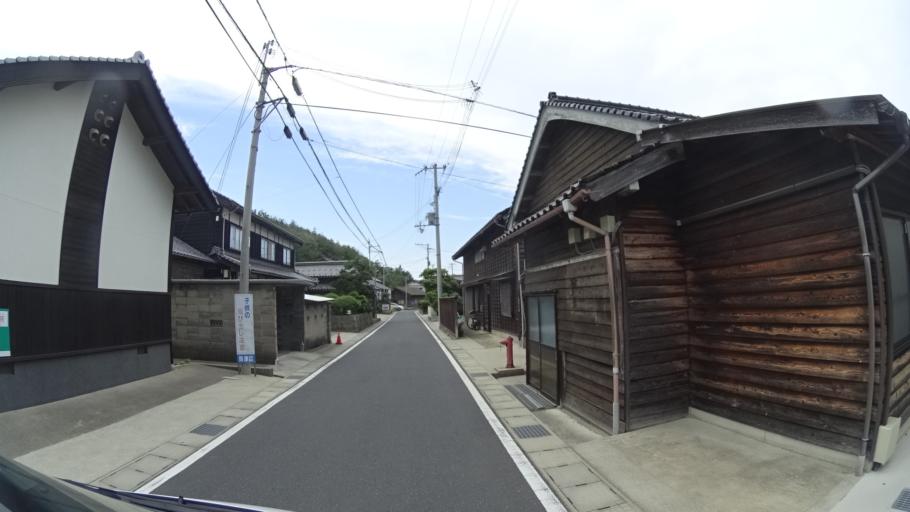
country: JP
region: Kyoto
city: Miyazu
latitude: 35.6998
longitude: 135.0539
